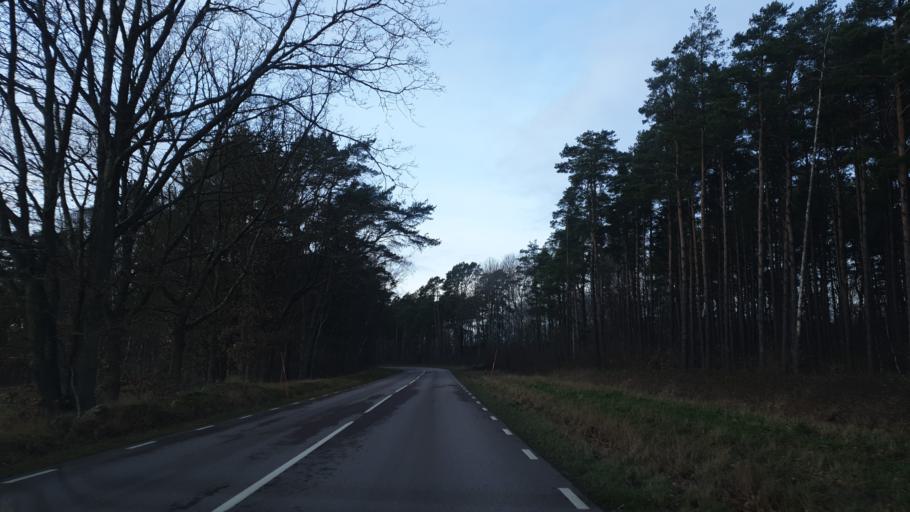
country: SE
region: Kalmar
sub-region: Torsas Kommun
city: Torsas
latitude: 56.2537
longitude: 16.0172
